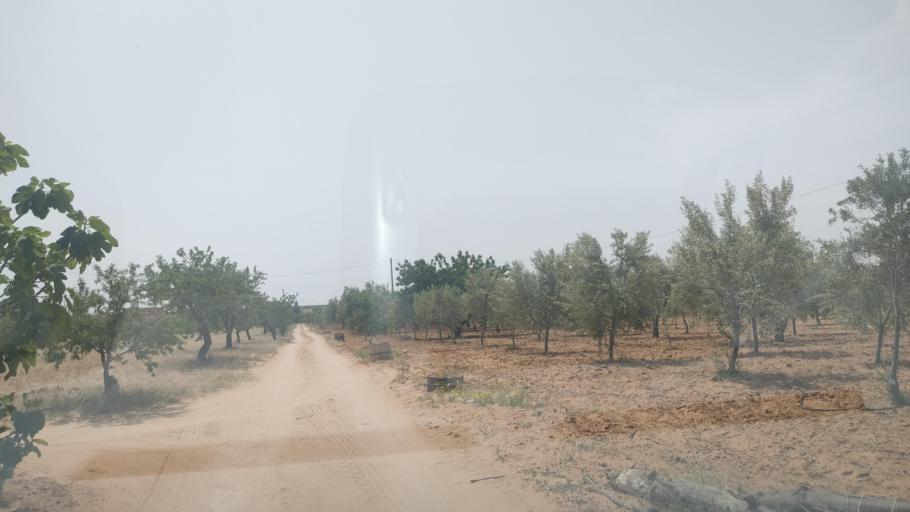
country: TN
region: Safaqis
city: Sfax
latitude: 34.8435
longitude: 10.5866
